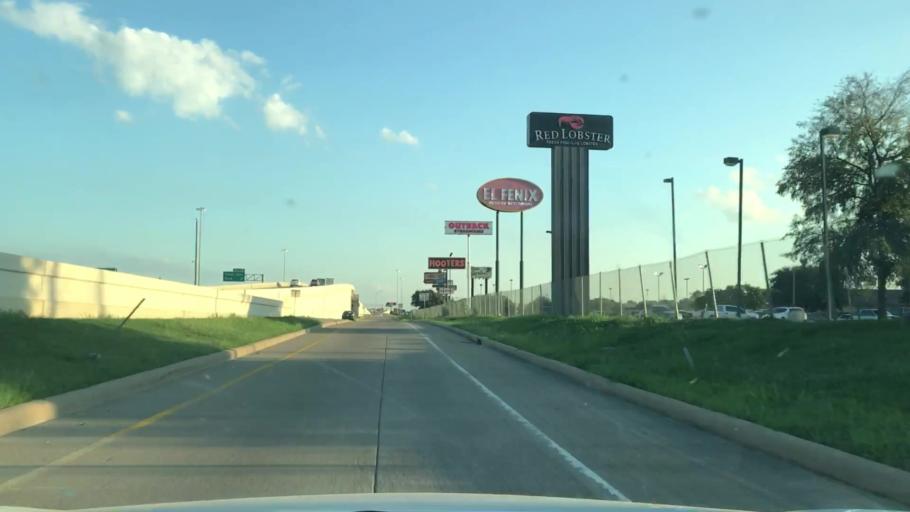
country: US
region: Texas
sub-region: Dallas County
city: Mesquite
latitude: 32.8193
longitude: -96.6295
